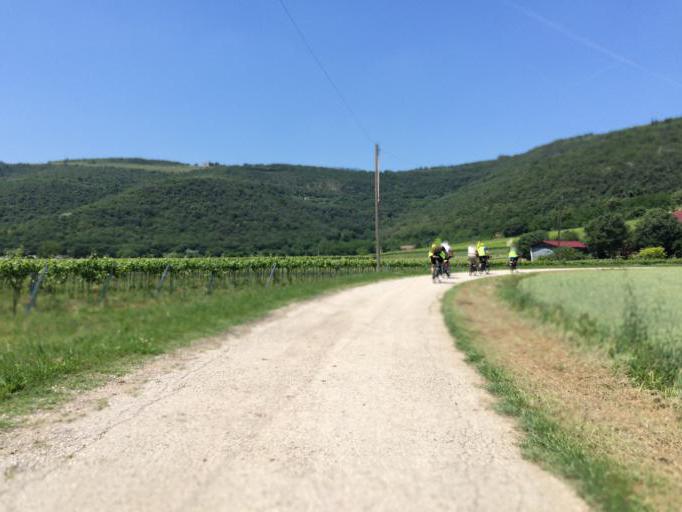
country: IT
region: Veneto
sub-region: Provincia di Vicenza
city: Villaga
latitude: 45.3943
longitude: 11.5309
